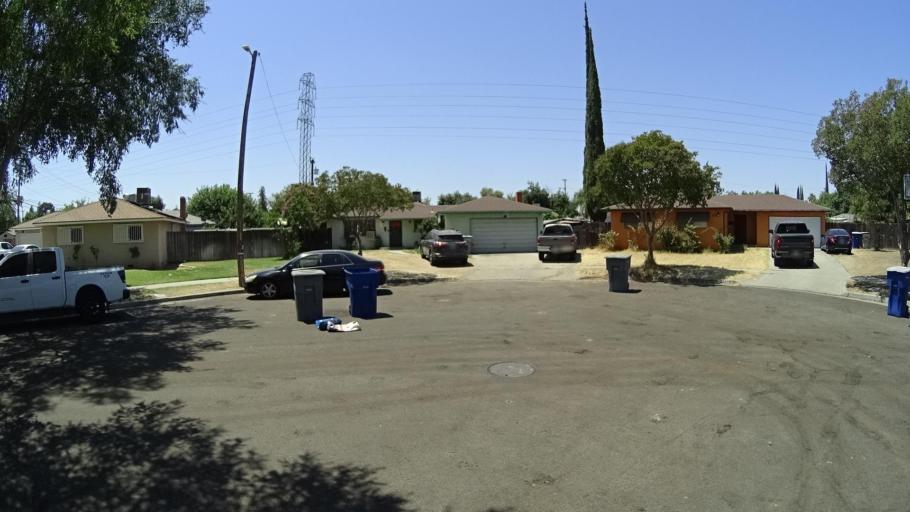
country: US
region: California
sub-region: Fresno County
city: Sunnyside
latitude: 36.7600
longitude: -119.7277
